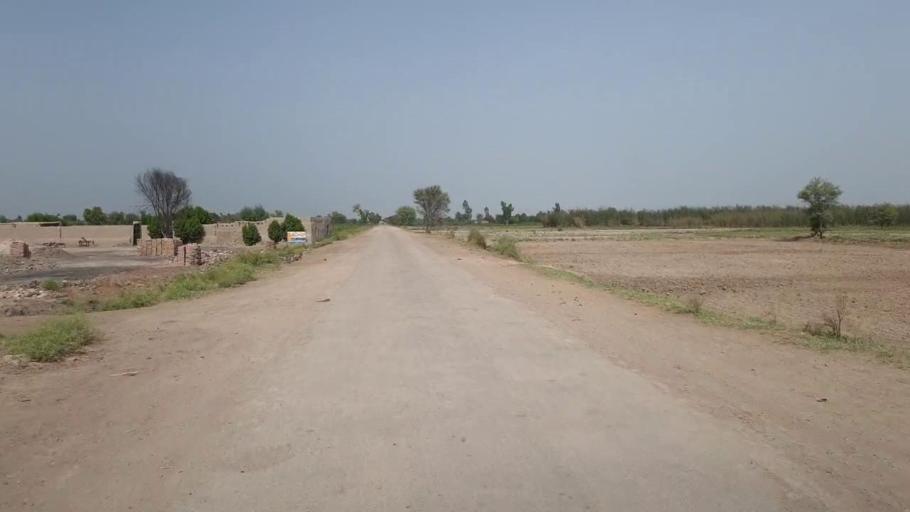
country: PK
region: Sindh
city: Daulatpur
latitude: 26.5486
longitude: 68.0023
